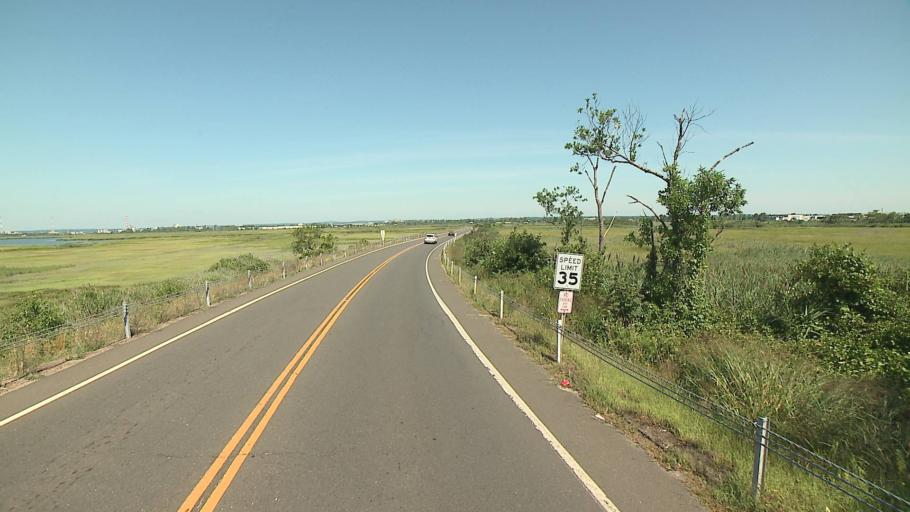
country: US
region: Connecticut
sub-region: Fairfield County
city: Stratford
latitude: 41.1531
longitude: -73.1326
